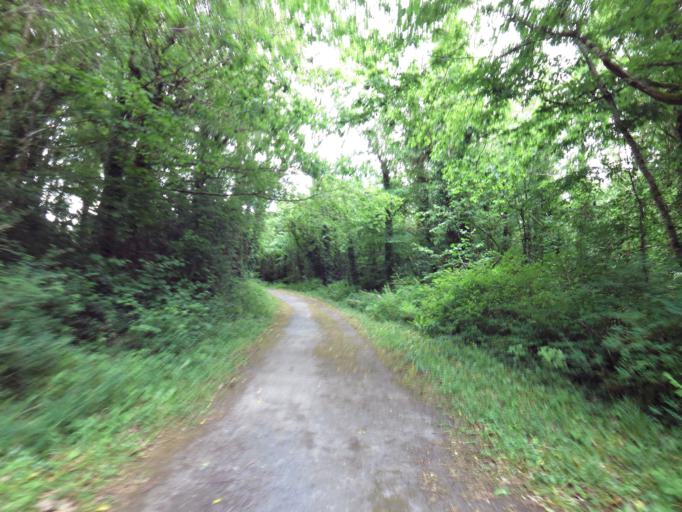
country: IE
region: Connaught
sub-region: County Galway
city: Gort
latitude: 53.0810
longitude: -8.8681
